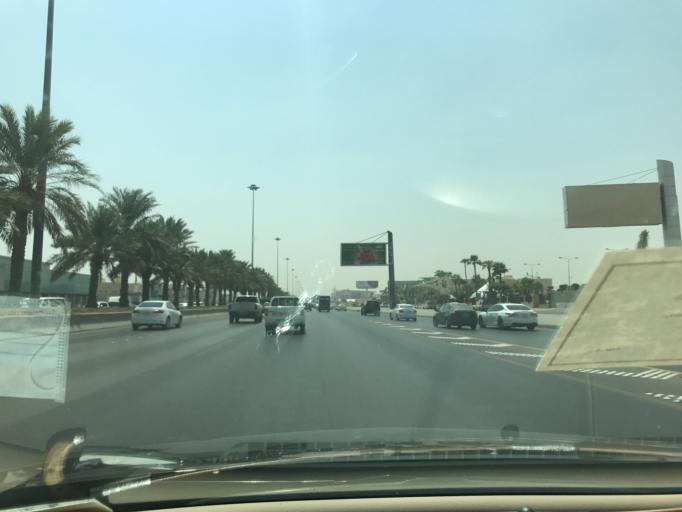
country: SA
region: Ar Riyad
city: Riyadh
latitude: 24.7527
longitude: 46.7423
